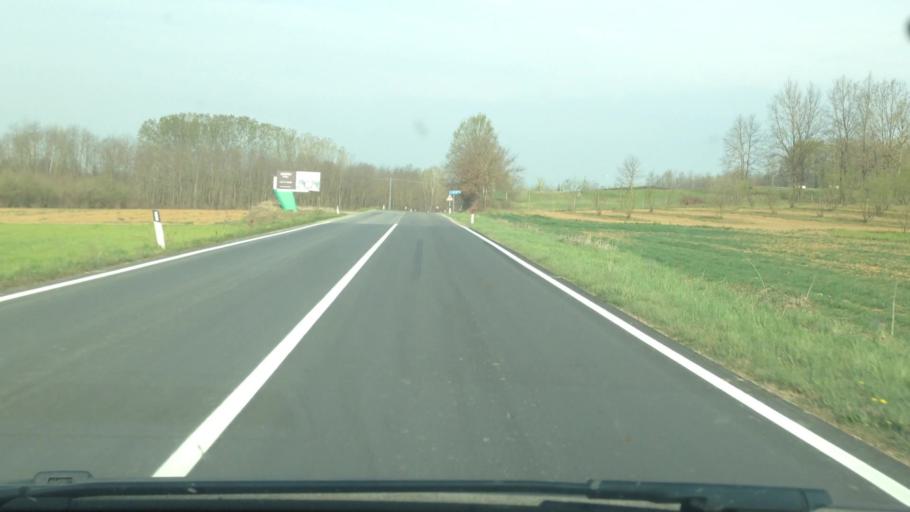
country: IT
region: Piedmont
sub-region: Provincia di Cuneo
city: Monta
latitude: 44.8285
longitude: 7.9322
